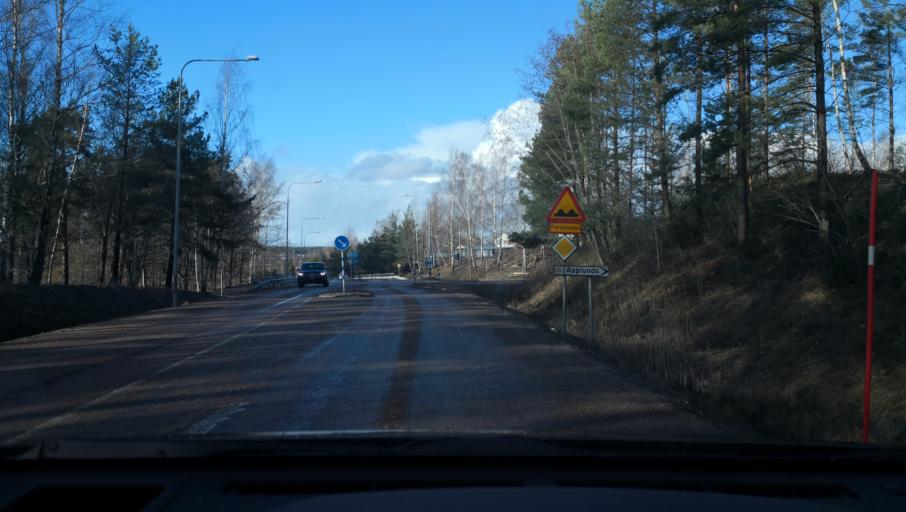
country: SE
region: Vaestmanland
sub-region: Arboga Kommun
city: Arboga
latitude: 59.3841
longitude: 15.8391
